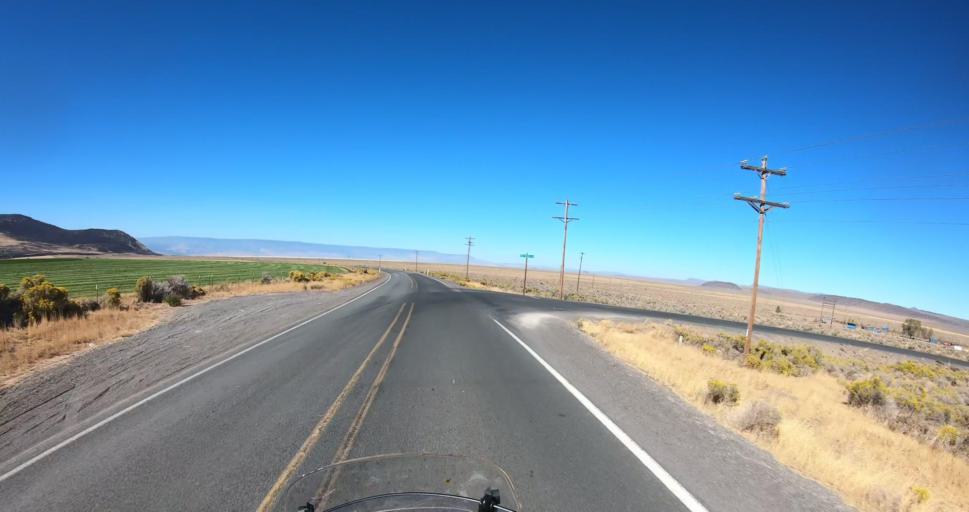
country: US
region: Oregon
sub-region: Lake County
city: Lakeview
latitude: 42.7042
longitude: -120.5486
